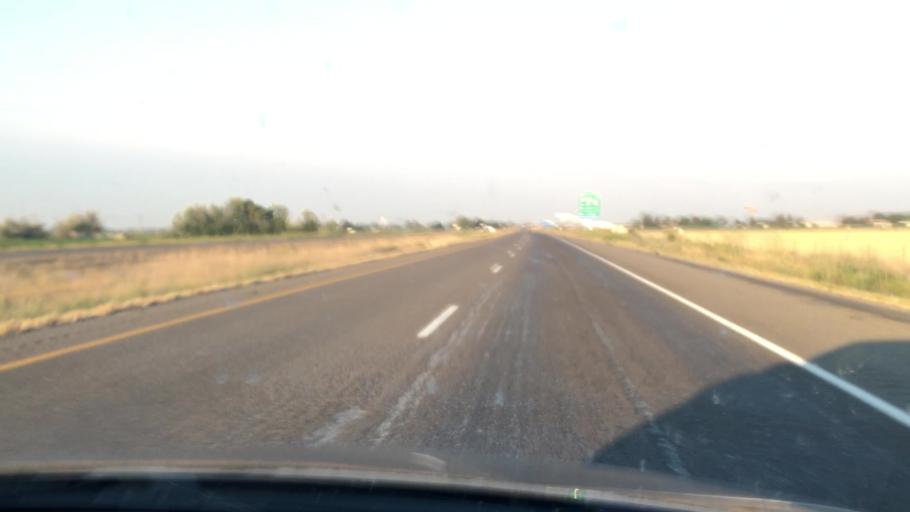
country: US
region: Idaho
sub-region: Minidoka County
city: Heyburn
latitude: 42.5681
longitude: -113.7576
